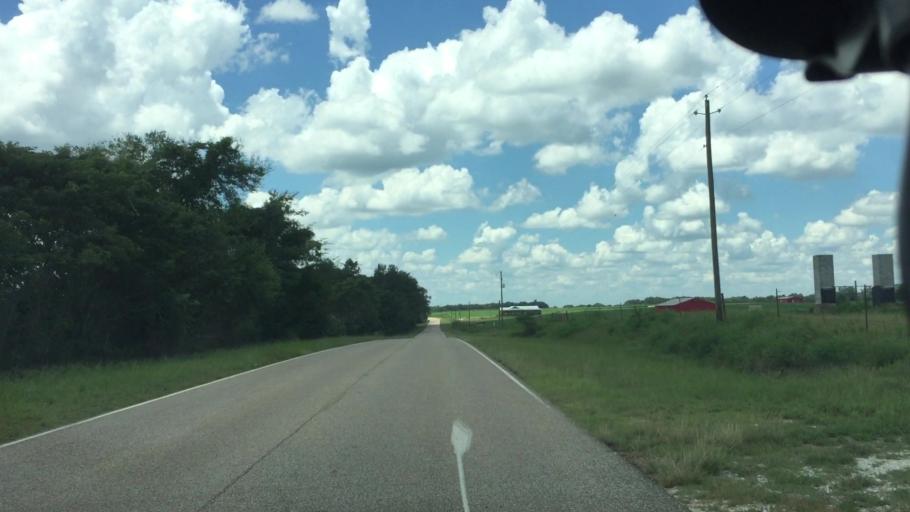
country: US
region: Alabama
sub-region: Coffee County
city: New Brockton
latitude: 31.4150
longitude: -85.8729
